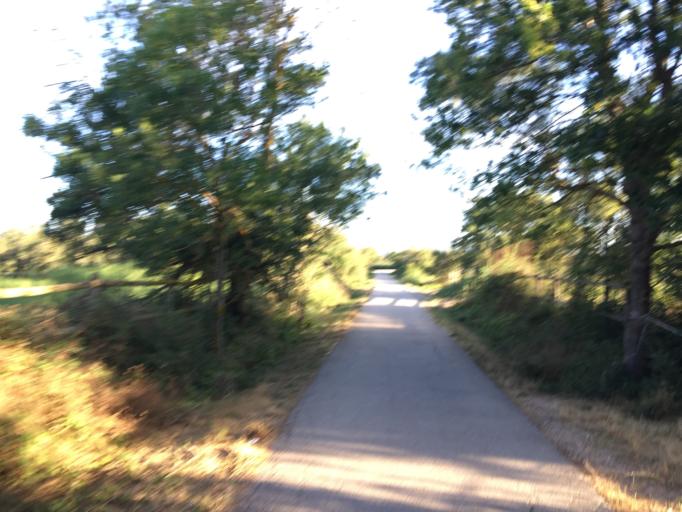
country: ES
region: Catalonia
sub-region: Provincia de Girona
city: Empuriabrava
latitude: 42.2589
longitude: 3.1191
